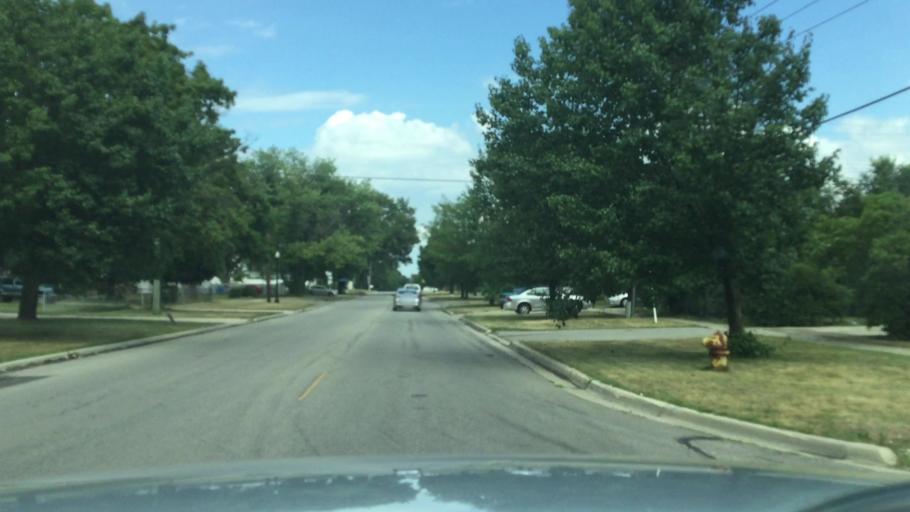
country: US
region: Michigan
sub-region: Washtenaw County
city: Ypsilanti
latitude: 42.2318
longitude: -83.5724
